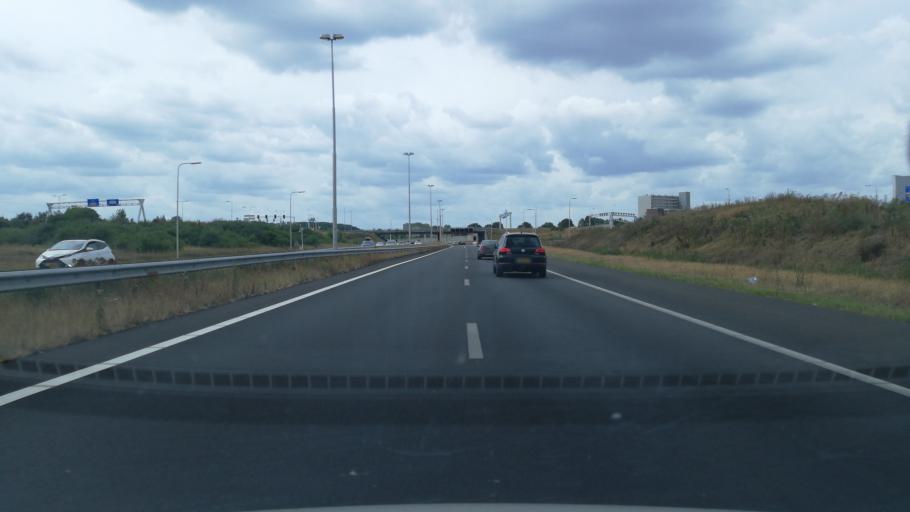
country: NL
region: Limburg
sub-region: Gemeente Roerdalen
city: Melick
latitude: 51.1829
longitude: 6.0214
